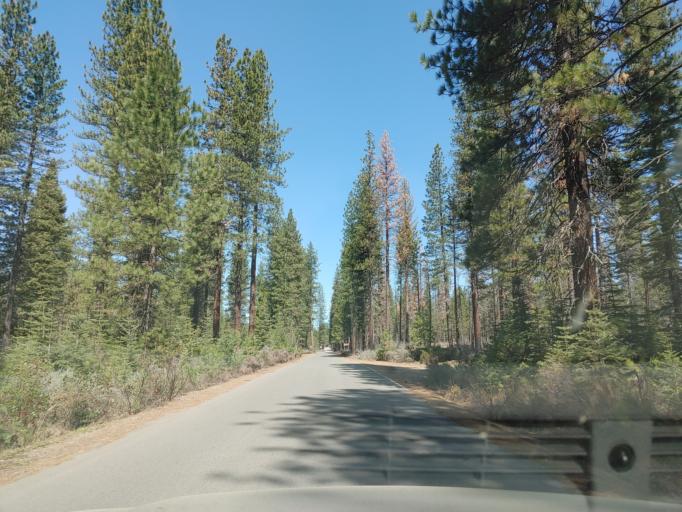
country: US
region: California
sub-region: Siskiyou County
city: McCloud
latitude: 41.2618
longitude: -121.9426
